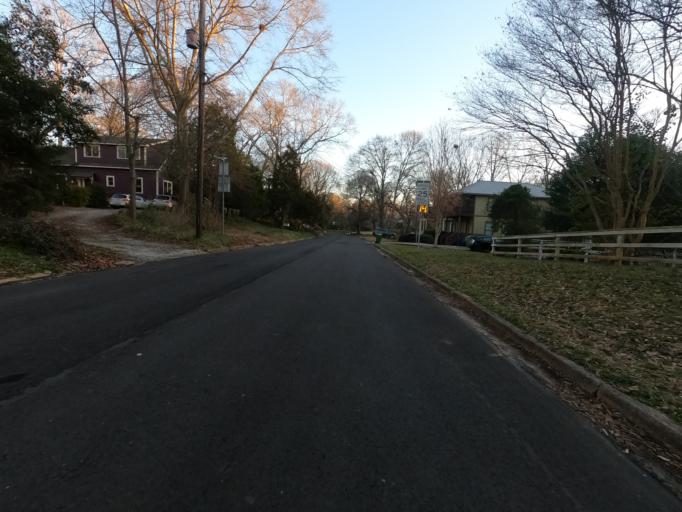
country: US
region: Georgia
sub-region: Clarke County
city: Athens
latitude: 33.9568
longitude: -83.3639
